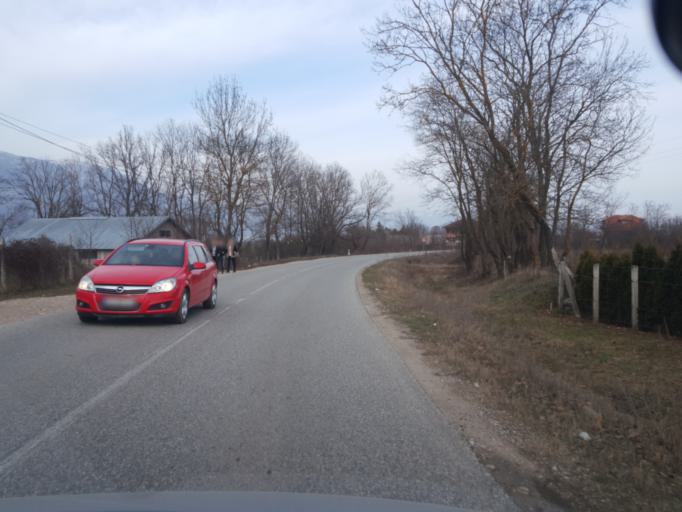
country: XK
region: Pec
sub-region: Komuna e Istogut
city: Istok
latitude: 42.7373
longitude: 20.4784
